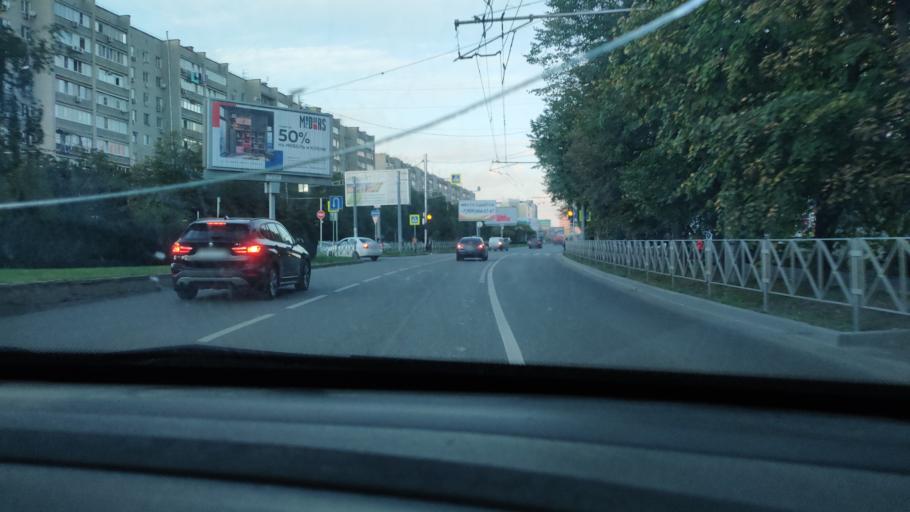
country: RU
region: Krasnodarskiy
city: Krasnodar
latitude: 45.0642
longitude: 38.9627
